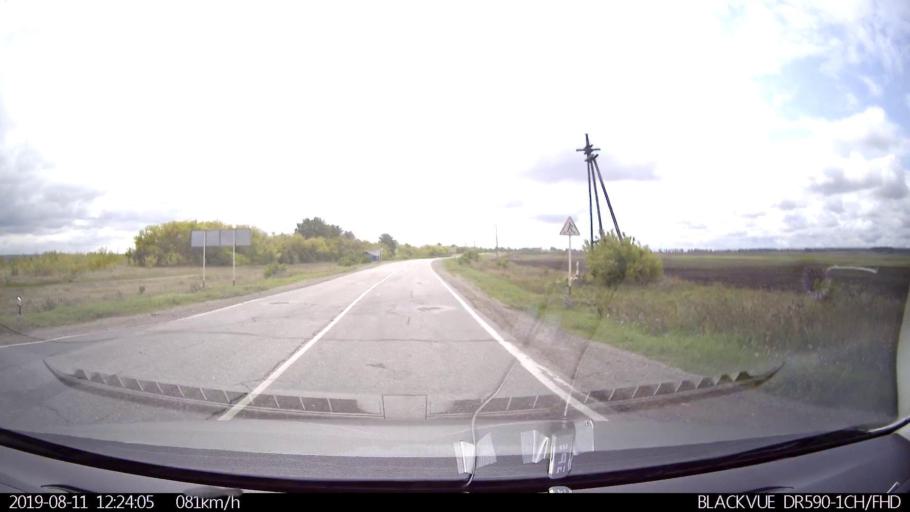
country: RU
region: Ulyanovsk
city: Ignatovka
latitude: 53.8875
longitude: 47.9501
